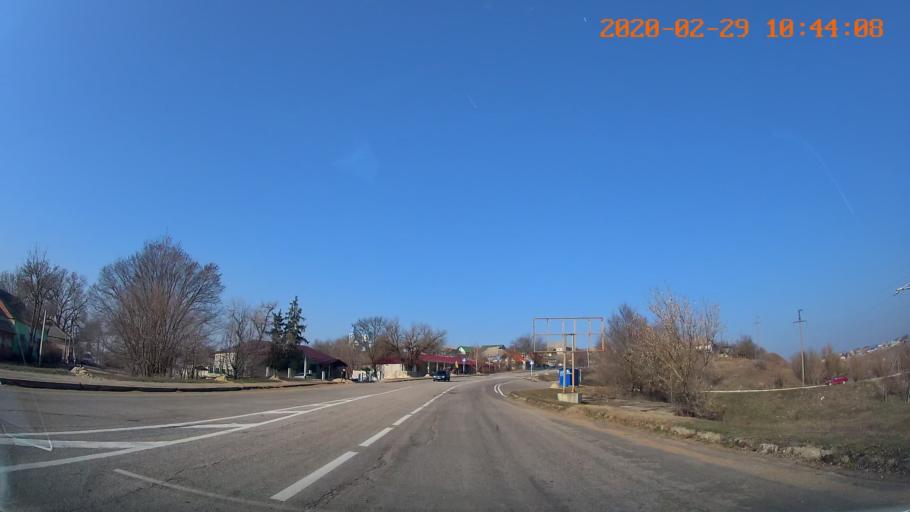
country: MD
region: Telenesti
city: Grigoriopol
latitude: 47.0680
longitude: 29.3982
